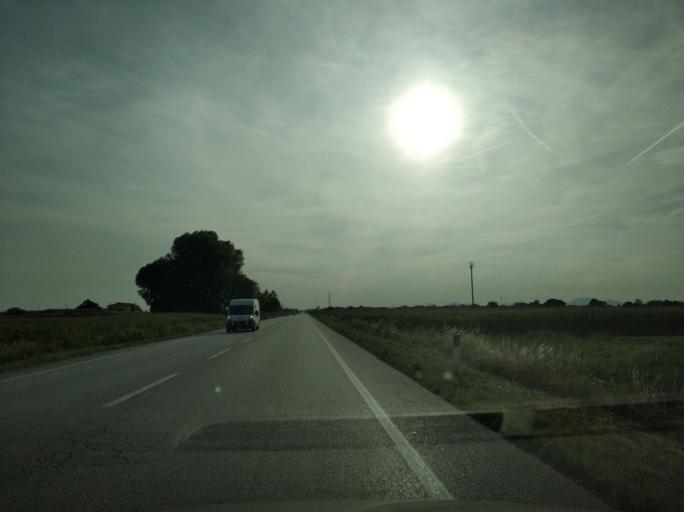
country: IT
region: Veneto
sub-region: Provincia di Padova
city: Candiana
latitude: 45.2133
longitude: 11.9944
